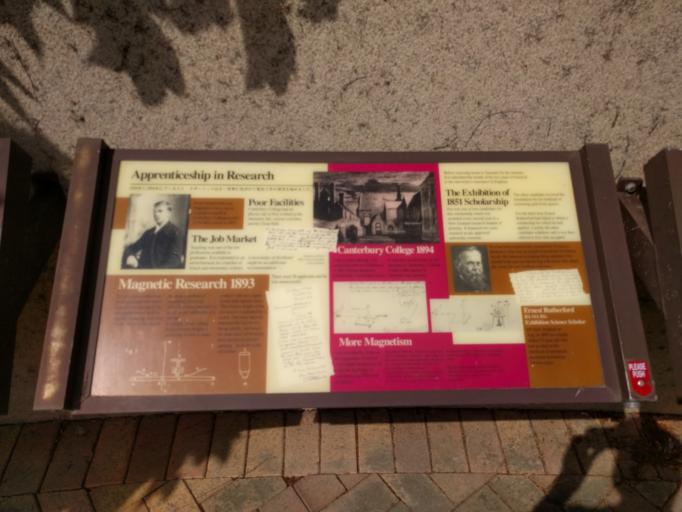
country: NZ
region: Tasman
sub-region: Tasman District
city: Brightwater
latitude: -41.3773
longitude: 173.1018
